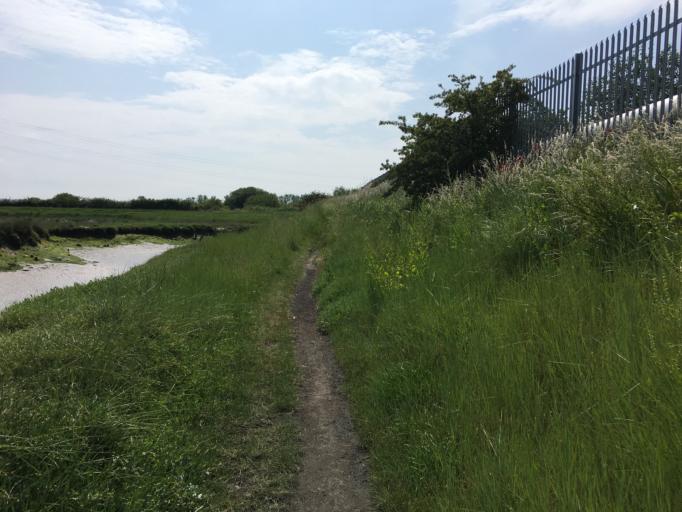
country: GB
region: England
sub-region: Kent
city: Sittingbourne
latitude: 51.3613
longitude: 0.7578
